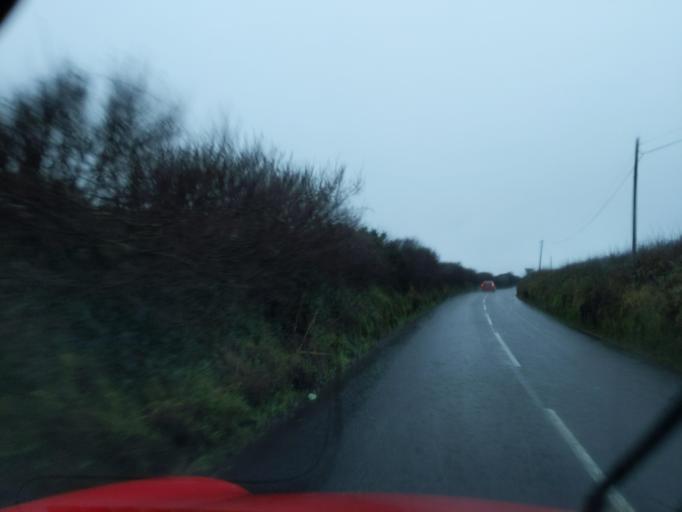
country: GB
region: England
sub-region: Cornwall
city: Camelford
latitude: 50.6394
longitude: -4.6931
